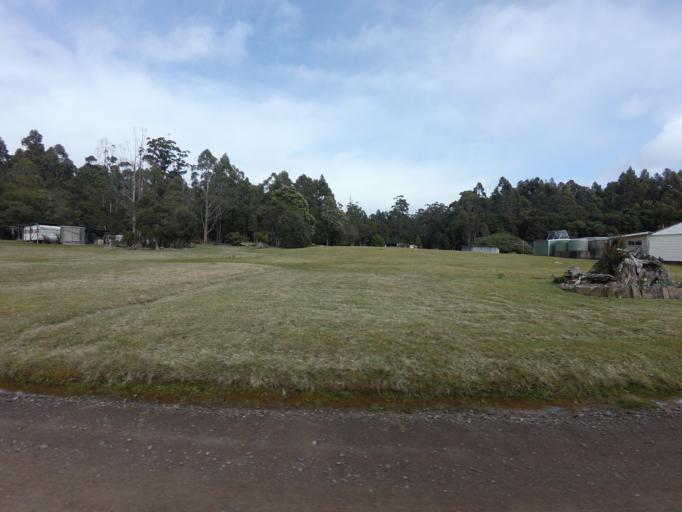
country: AU
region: Tasmania
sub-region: Huon Valley
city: Geeveston
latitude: -43.5375
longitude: 146.8914
